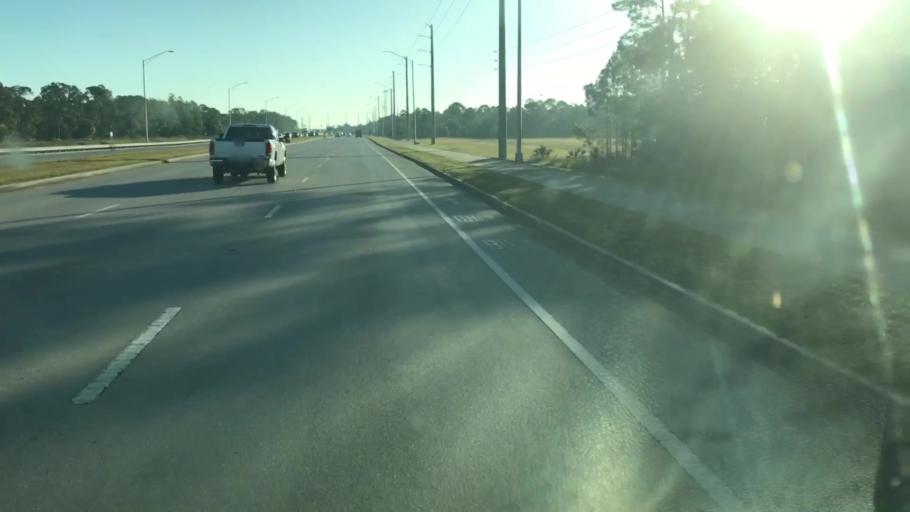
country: US
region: Florida
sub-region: Collier County
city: Orangetree
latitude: 26.2760
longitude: -81.6133
